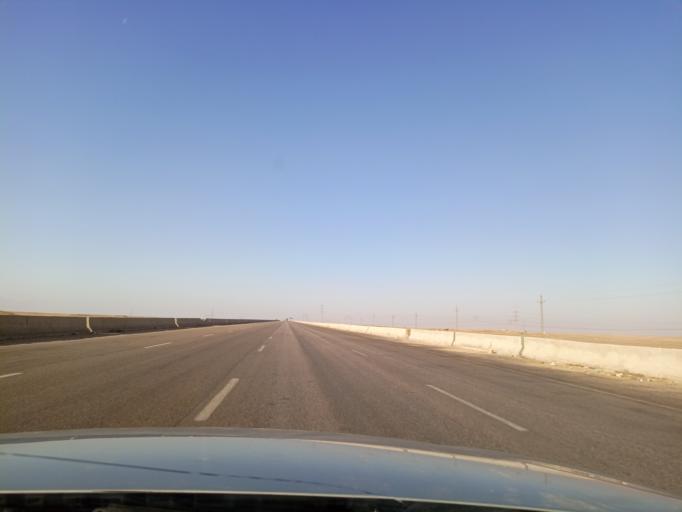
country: EG
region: Muhafazat al Fayyum
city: Tamiyah
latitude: 29.6350
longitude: 30.9810
